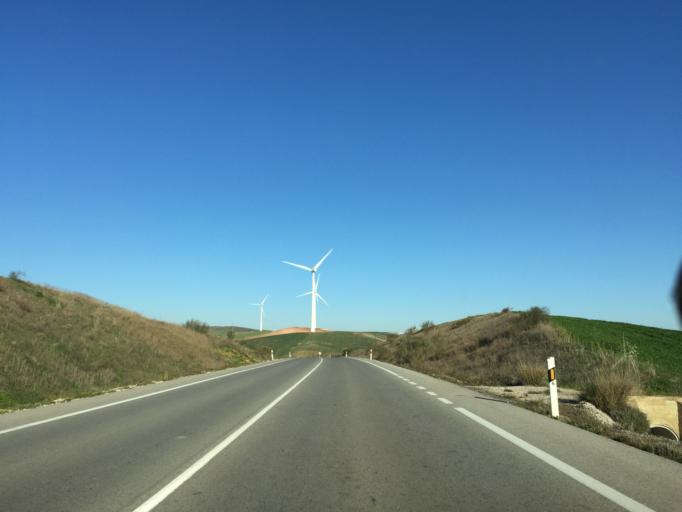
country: ES
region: Andalusia
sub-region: Provincia de Malaga
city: Ardales
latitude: 36.9303
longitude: -4.8558
